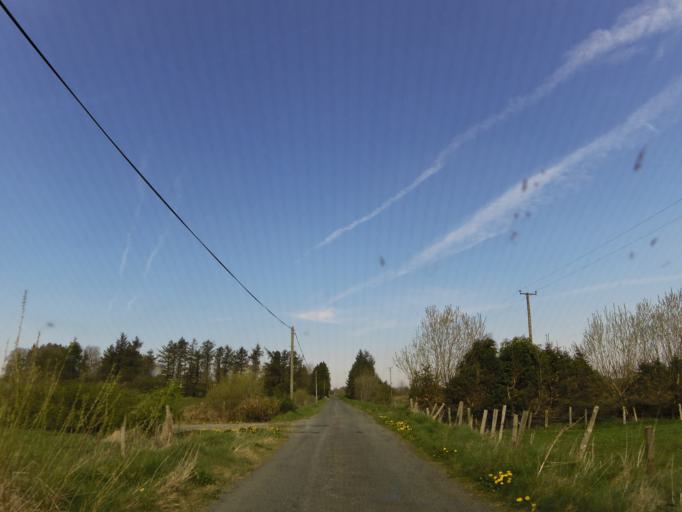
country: IE
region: Connaught
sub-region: Maigh Eo
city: Kiltamagh
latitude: 53.8095
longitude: -8.9767
